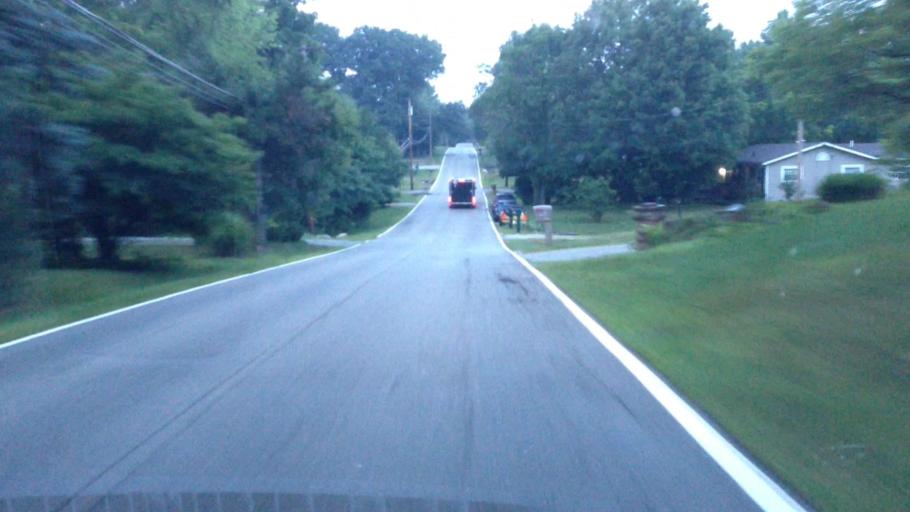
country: US
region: Ohio
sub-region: Summit County
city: Silver Lake
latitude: 41.1723
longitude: -81.4549
